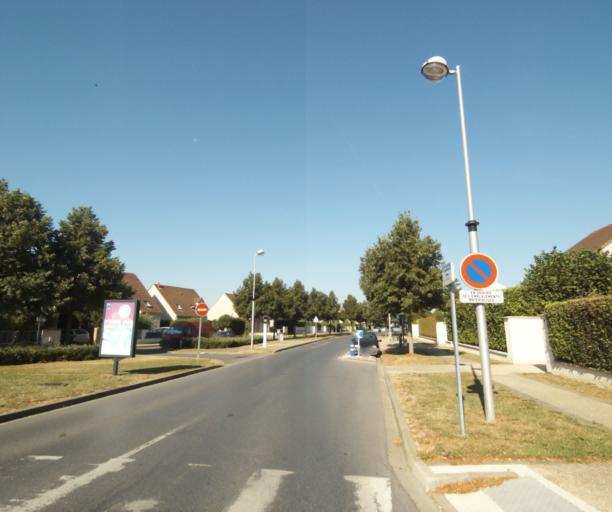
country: FR
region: Ile-de-France
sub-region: Departement de Seine-et-Marne
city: Moissy-Cramayel
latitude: 48.6315
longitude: 2.5845
